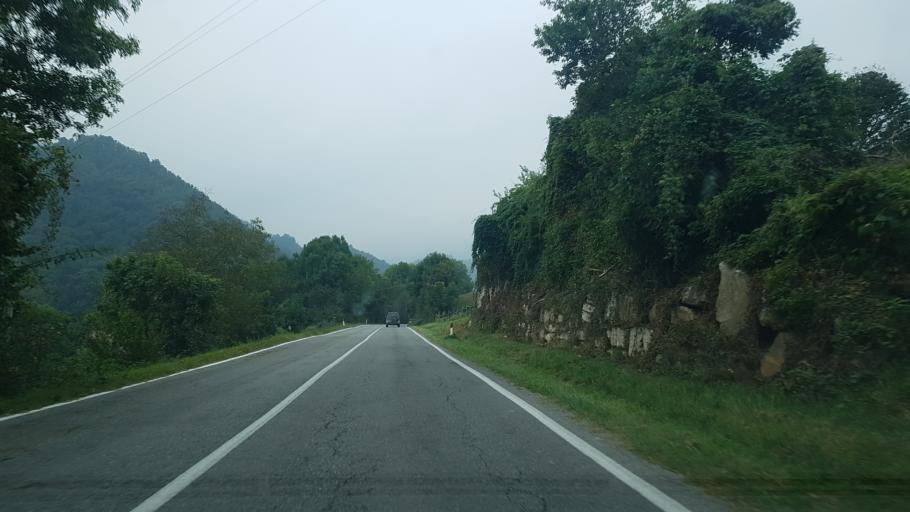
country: IT
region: Piedmont
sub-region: Provincia di Cuneo
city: Frabosa Sottana
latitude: 44.3156
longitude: 7.8036
